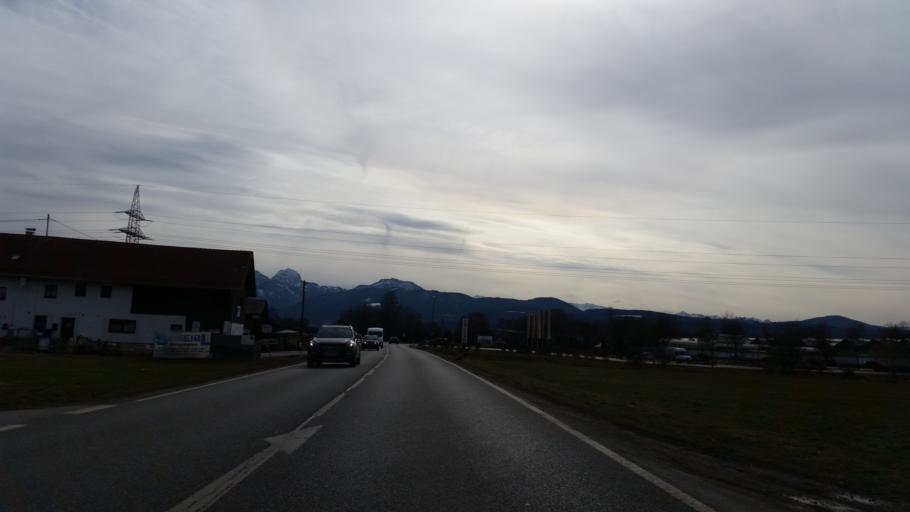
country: DE
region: Bavaria
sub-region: Upper Bavaria
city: Bad Aibling
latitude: 47.8426
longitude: 12.0123
